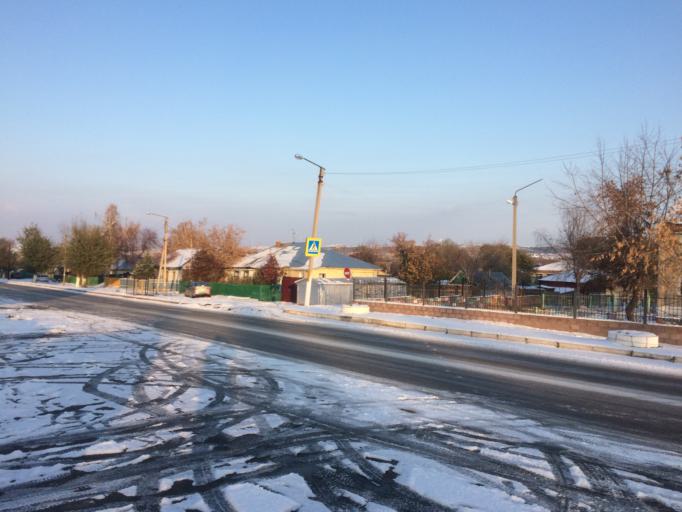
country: RU
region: Bashkortostan
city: Abzakovo
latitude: 53.3398
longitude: 58.5071
